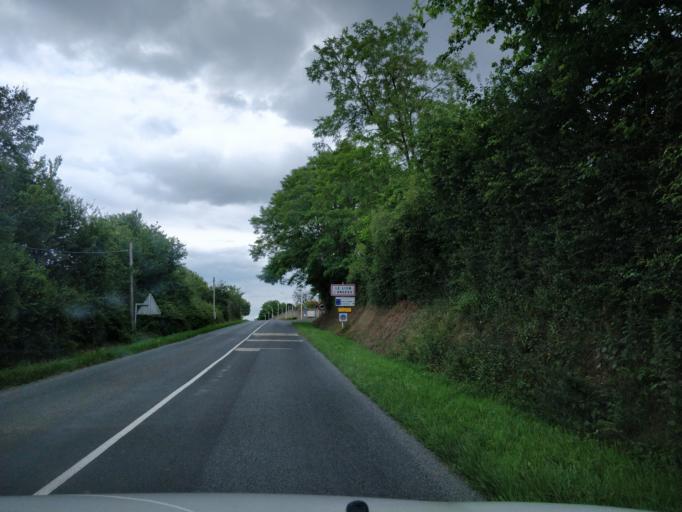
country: FR
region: Pays de la Loire
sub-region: Departement de Maine-et-Loire
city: Grez-Neuville
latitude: 47.6319
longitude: -0.7192
